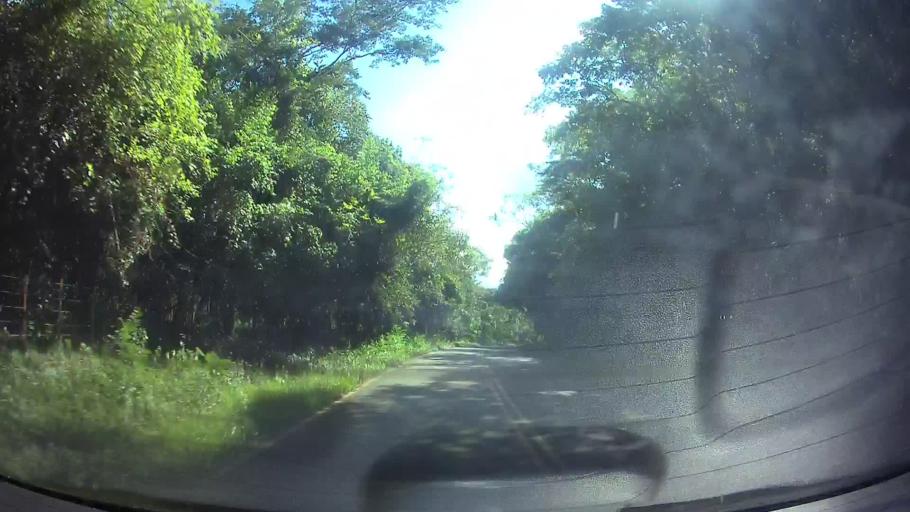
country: PY
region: Paraguari
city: Sapucai
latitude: -25.6683
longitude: -56.8586
